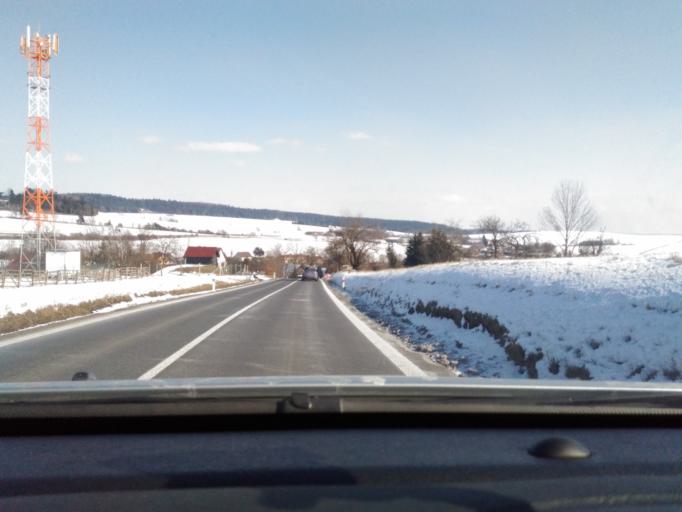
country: CZ
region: Vysocina
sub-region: Okres Zd'ar nad Sazavou
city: Nove Mesto na Morave
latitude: 49.5476
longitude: 16.1531
